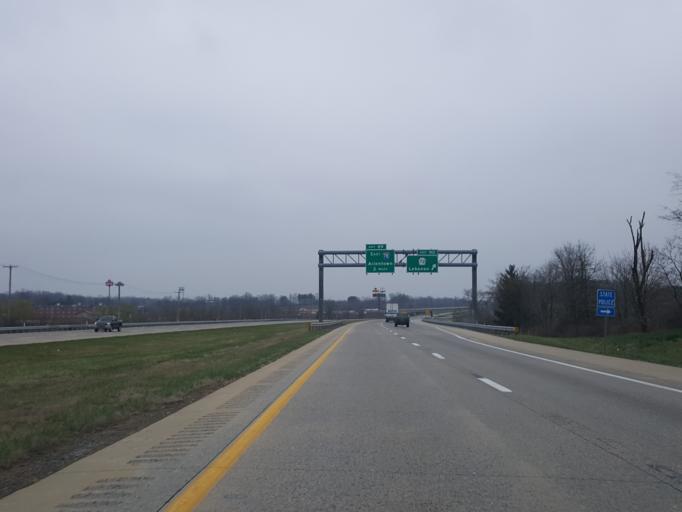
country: US
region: Pennsylvania
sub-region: Lebanon County
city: Jonestown
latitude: 40.4576
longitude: -76.5168
